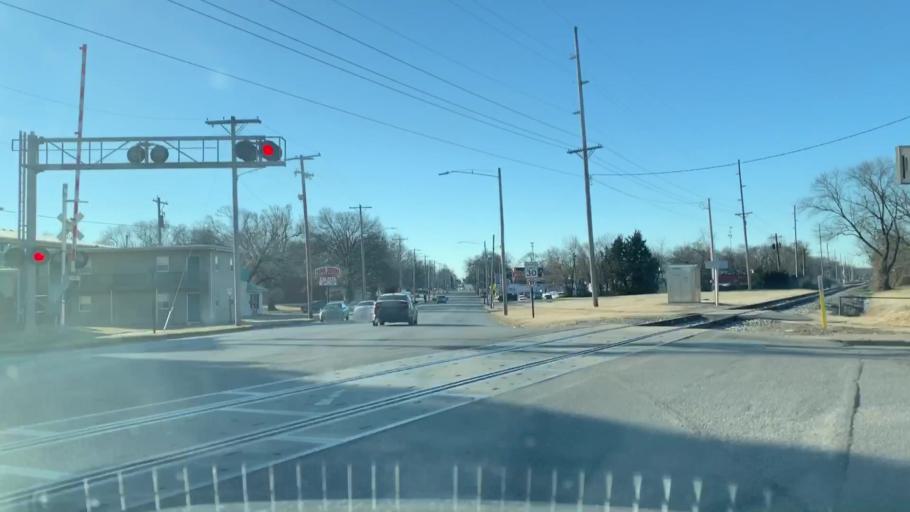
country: US
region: Kansas
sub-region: Crawford County
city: Pittsburg
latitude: 37.3944
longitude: -94.7051
